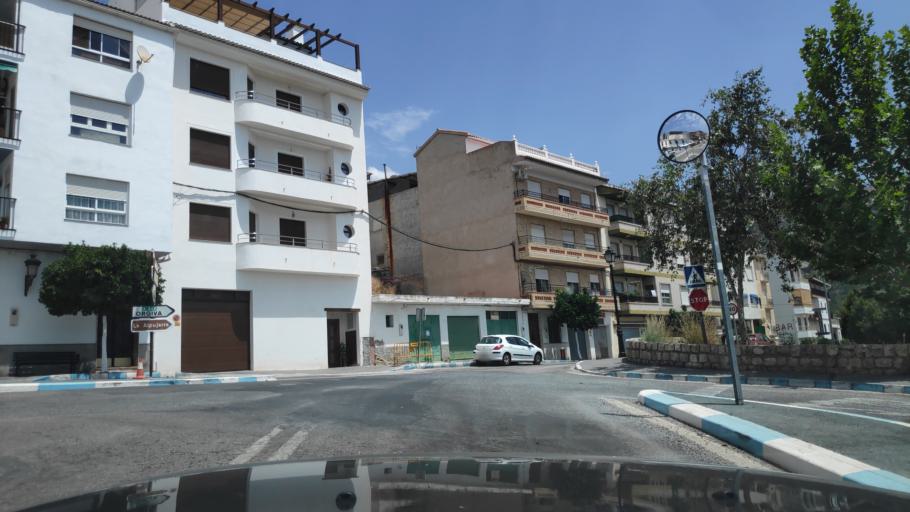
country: ES
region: Andalusia
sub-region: Provincia de Granada
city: Lanjaron
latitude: 36.9185
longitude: -3.4776
